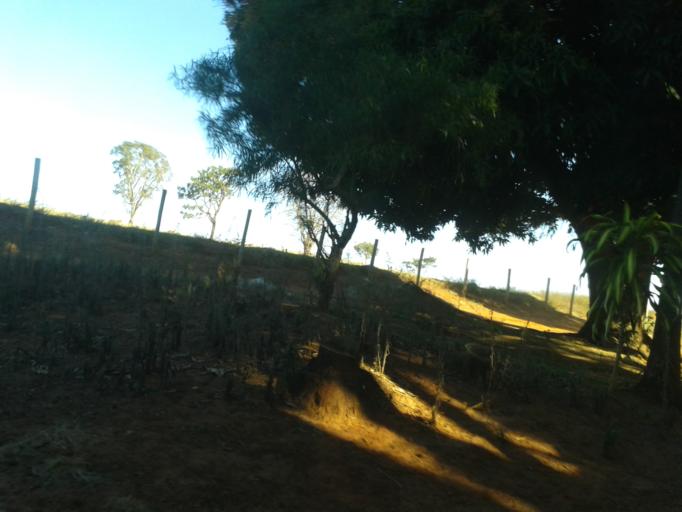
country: BR
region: Minas Gerais
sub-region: Centralina
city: Centralina
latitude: -18.7524
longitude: -49.1052
